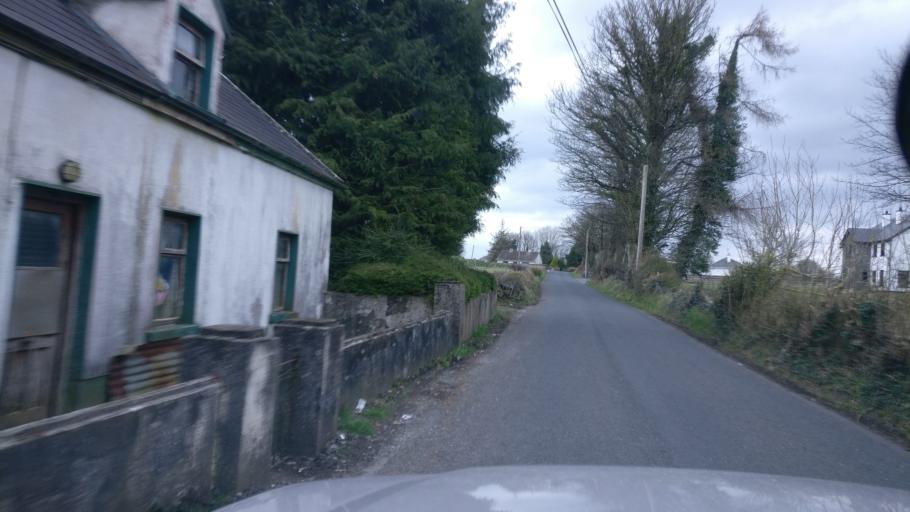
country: IE
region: Connaught
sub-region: County Galway
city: Loughrea
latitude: 53.2497
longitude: -8.5127
